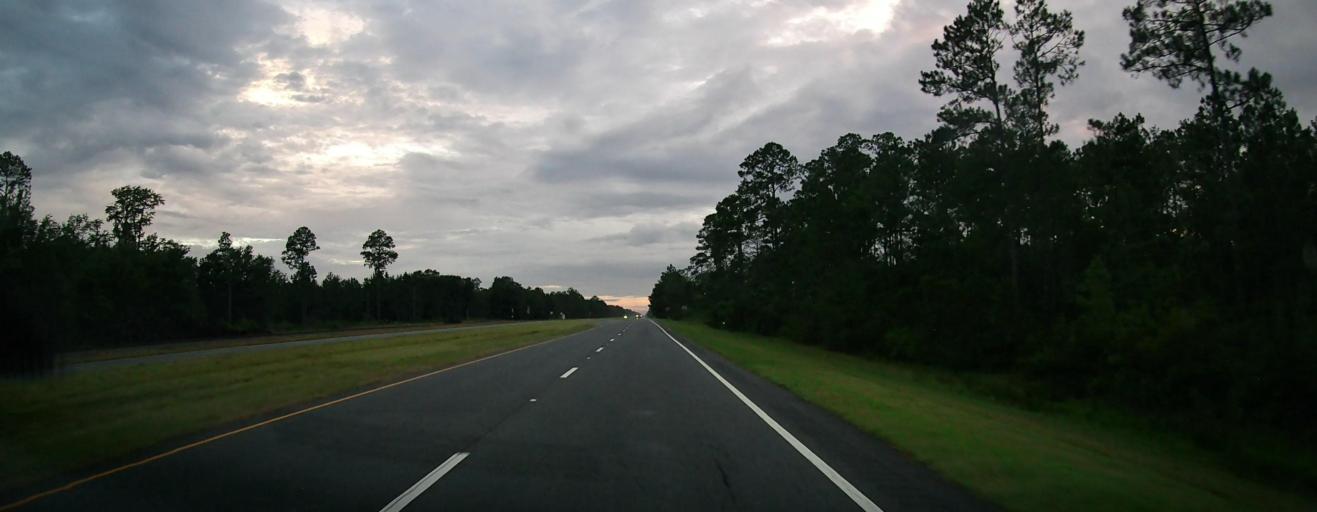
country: US
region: Georgia
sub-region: Lanier County
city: Lakeland
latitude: 30.8933
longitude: -83.1171
